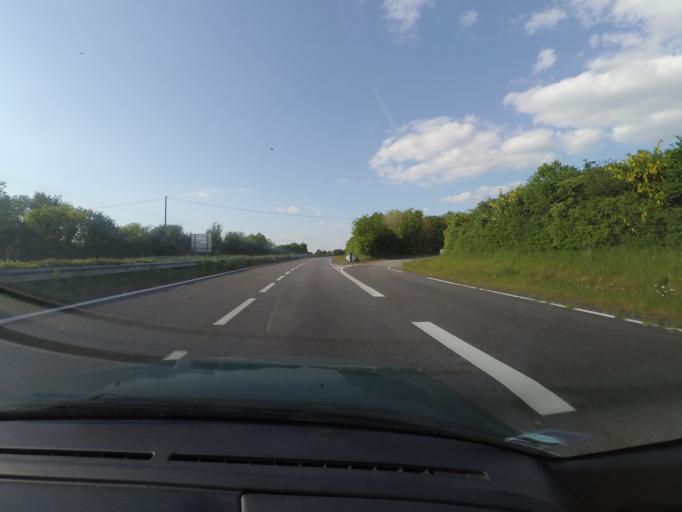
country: FR
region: Pays de la Loire
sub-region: Departement de la Vendee
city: Saligny
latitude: 46.8058
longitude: -1.4329
